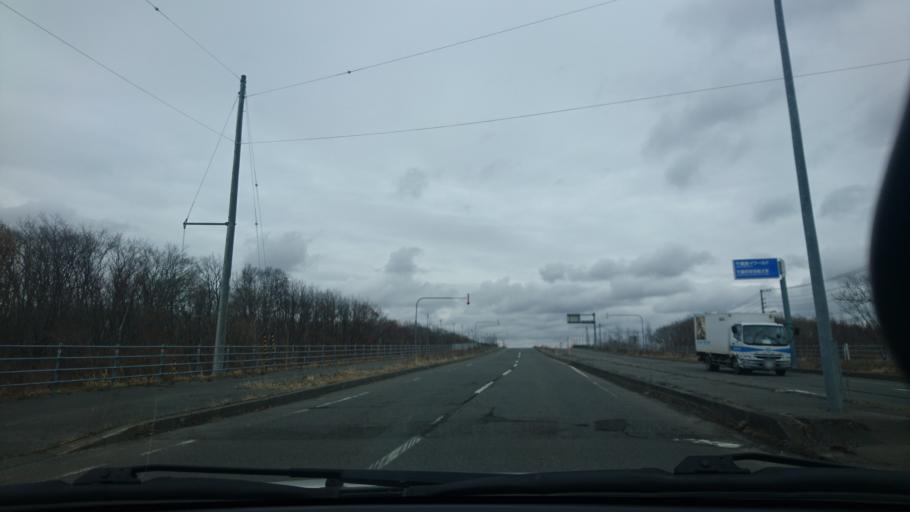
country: JP
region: Hokkaido
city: Chitose
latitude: 42.7969
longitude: 141.6910
